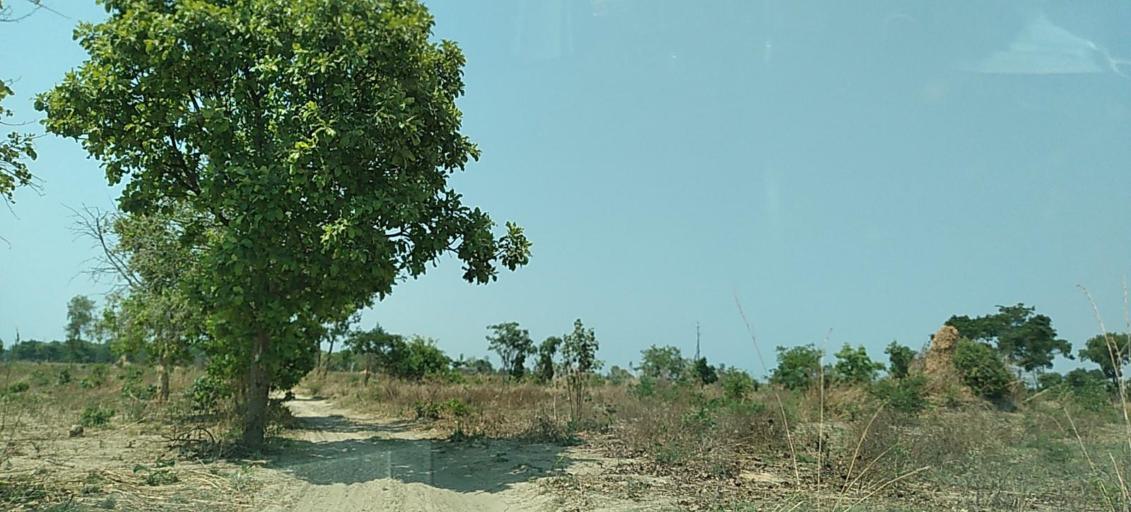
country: ZM
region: Copperbelt
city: Mpongwe
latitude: -13.8607
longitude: 28.0551
